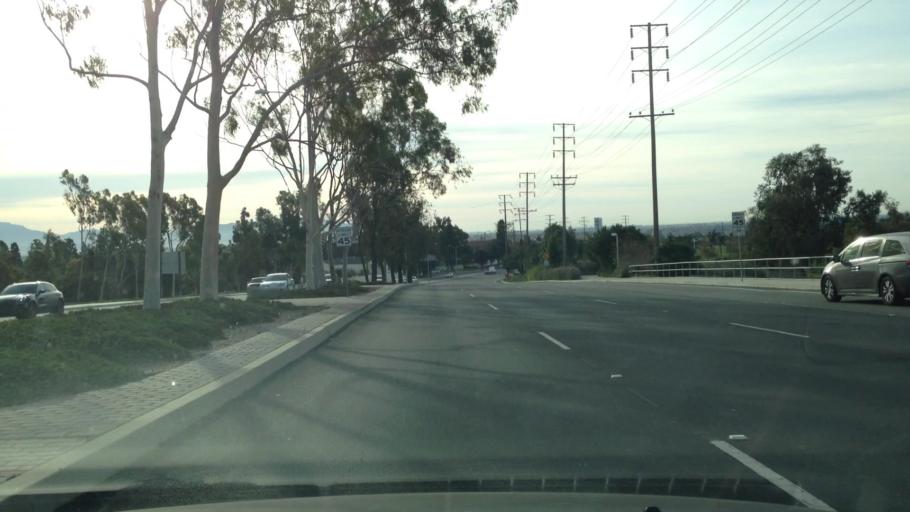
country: US
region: California
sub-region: Ventura County
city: Saticoy
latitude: 34.2741
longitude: -119.1905
